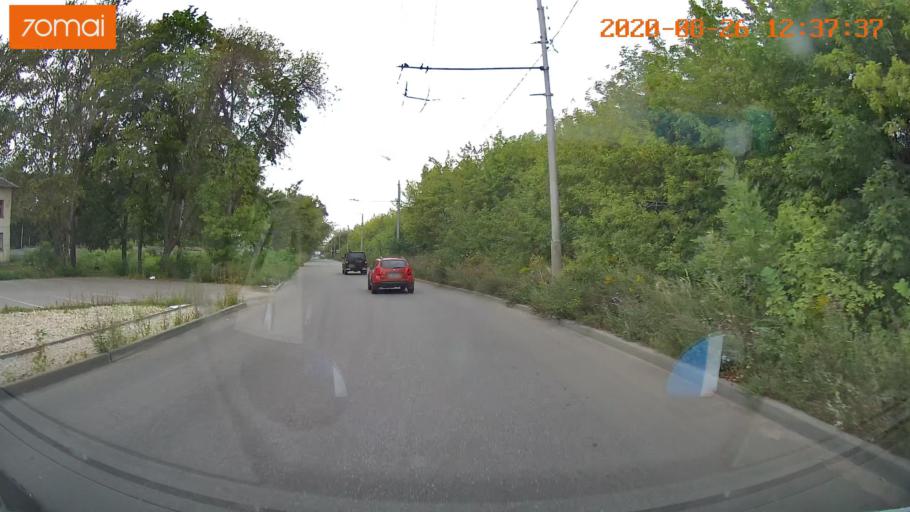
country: RU
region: Rjazan
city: Ryazan'
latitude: 54.6054
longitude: 39.7677
